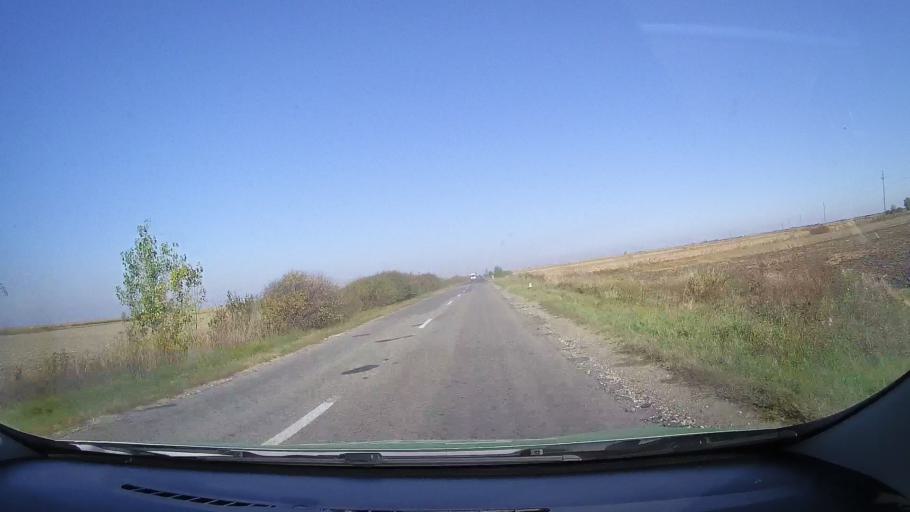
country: RO
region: Satu Mare
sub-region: Oras Tasnad
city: Tasnad
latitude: 47.5174
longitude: 22.5715
